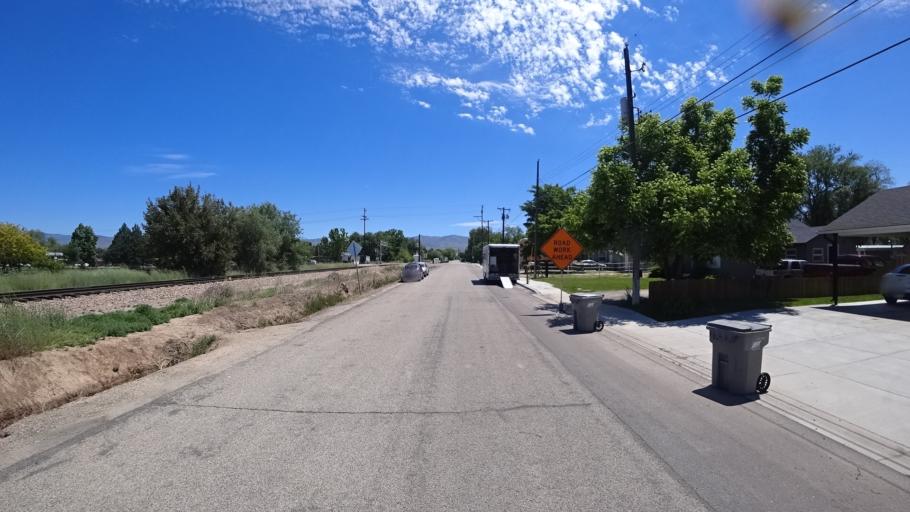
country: US
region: Idaho
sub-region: Ada County
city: Garden City
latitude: 43.6043
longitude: -116.2299
